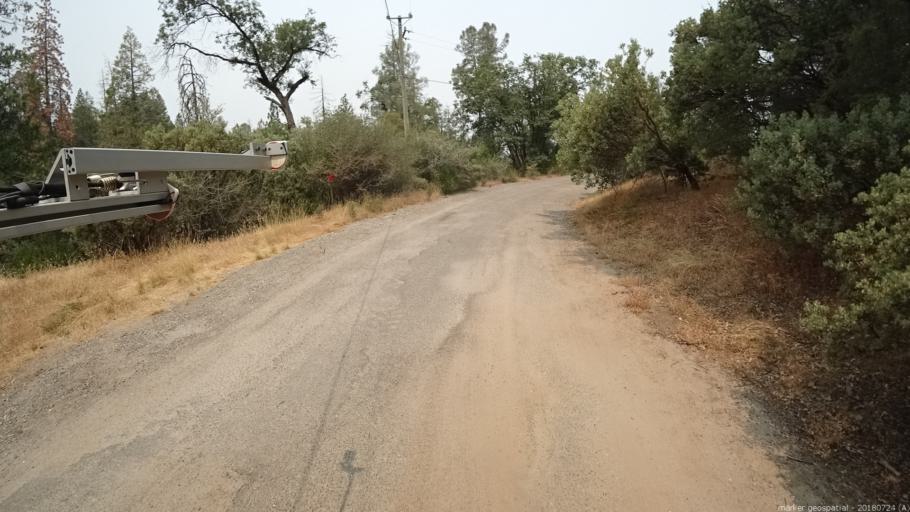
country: US
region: California
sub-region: Madera County
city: Oakhurst
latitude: 37.3259
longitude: -119.5943
